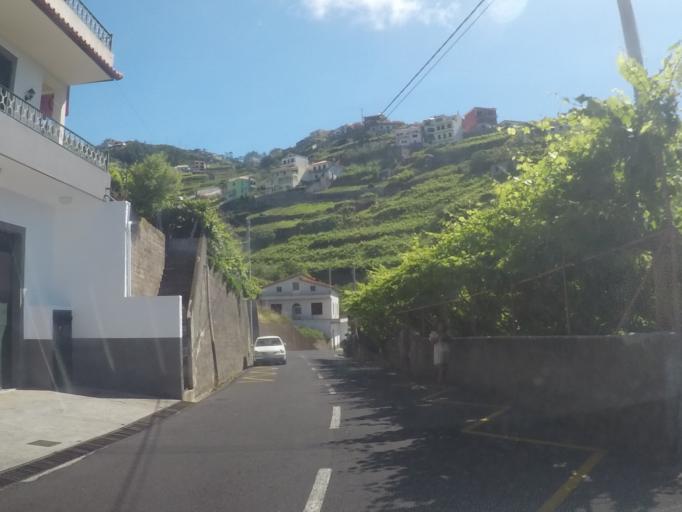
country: PT
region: Madeira
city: Camara de Lobos
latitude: 32.6727
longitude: -16.9717
